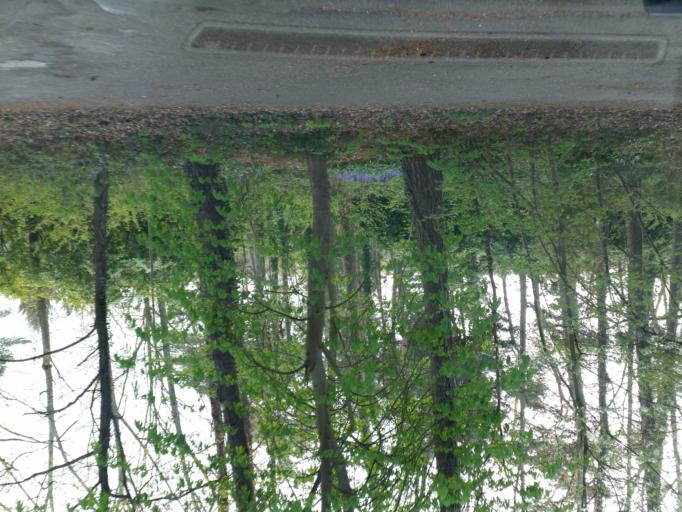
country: BE
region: Flanders
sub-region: Provincie Antwerpen
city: Bonheiden
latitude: 50.9825
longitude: 4.5181
